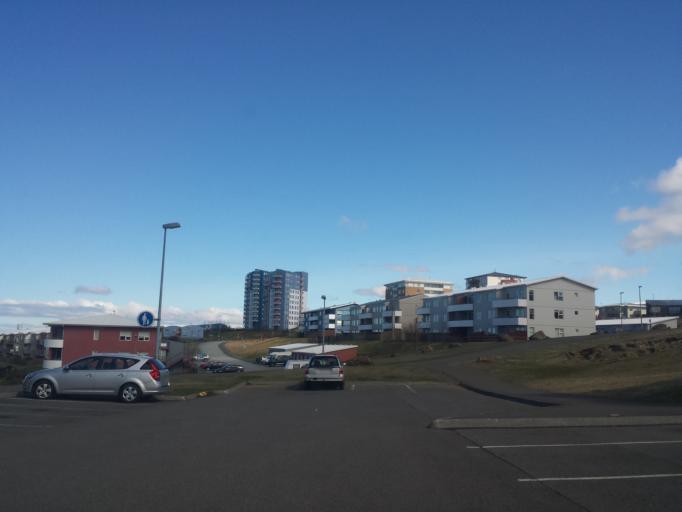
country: IS
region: Capital Region
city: Reykjavik
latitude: 64.0916
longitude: -21.8529
